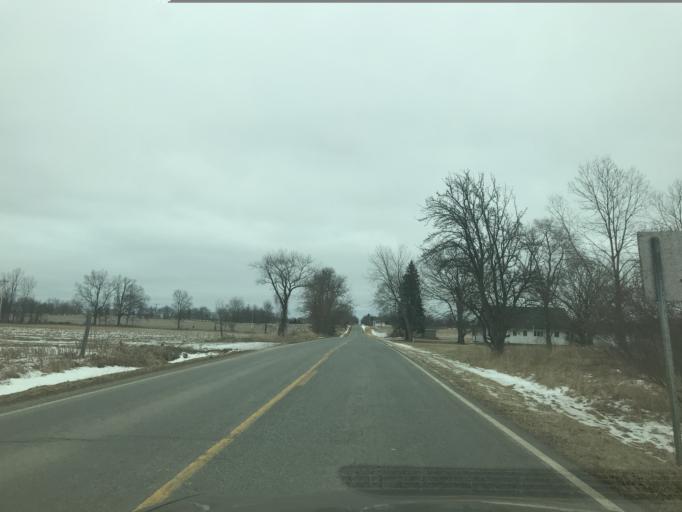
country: US
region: Michigan
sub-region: Jackson County
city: Brooklyn
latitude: 42.0734
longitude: -84.3481
